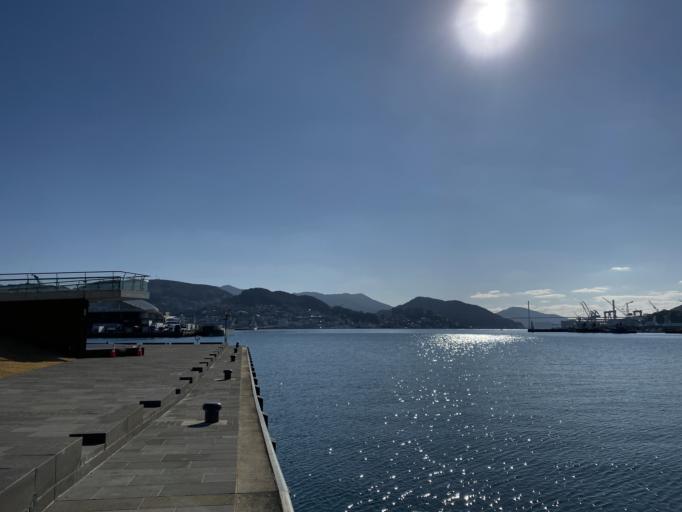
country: JP
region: Nagasaki
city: Nagasaki-shi
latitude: 32.7494
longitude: 129.8670
